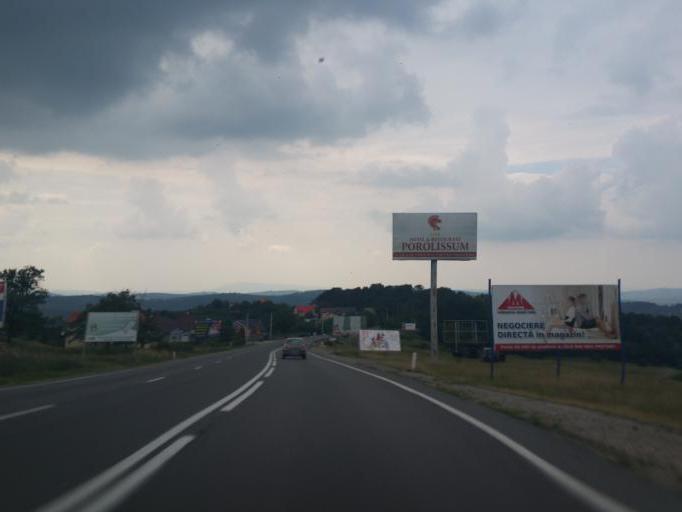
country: RO
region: Salaj
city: Zalau
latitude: 47.1611
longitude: 23.0884
